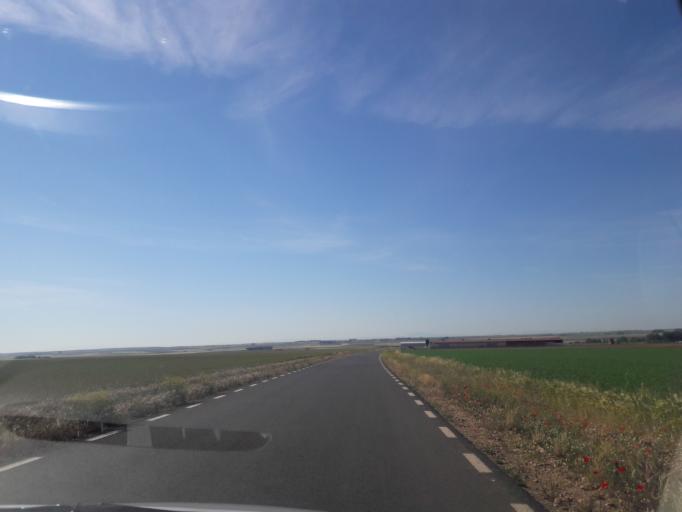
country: ES
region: Castille and Leon
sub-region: Provincia de Salamanca
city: Espino de la Orbada
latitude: 41.1186
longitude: -5.4270
